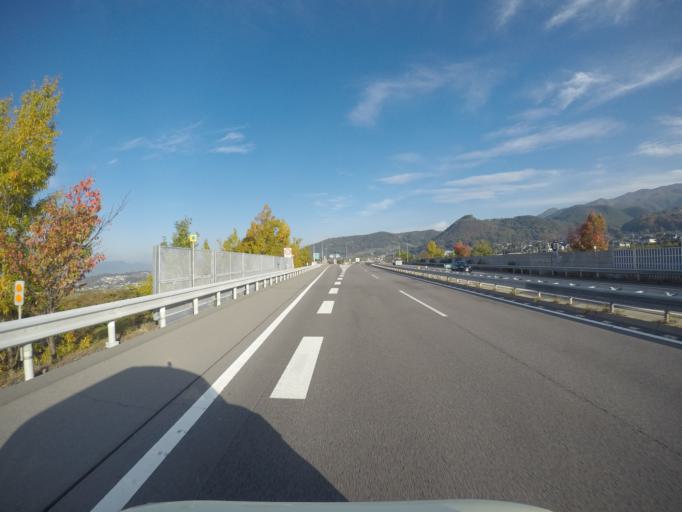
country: JP
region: Nagano
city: Ueda
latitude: 36.3681
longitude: 138.3494
